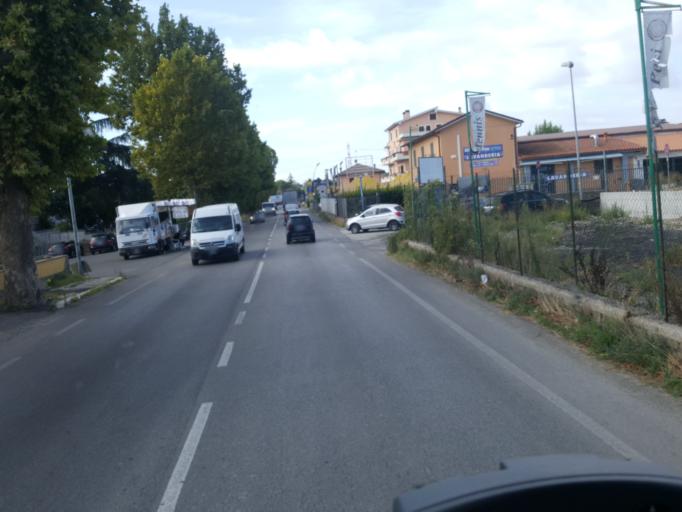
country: IT
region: Latium
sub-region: Citta metropolitana di Roma Capitale
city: Bivio di Capanelle
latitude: 42.1198
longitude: 12.5902
